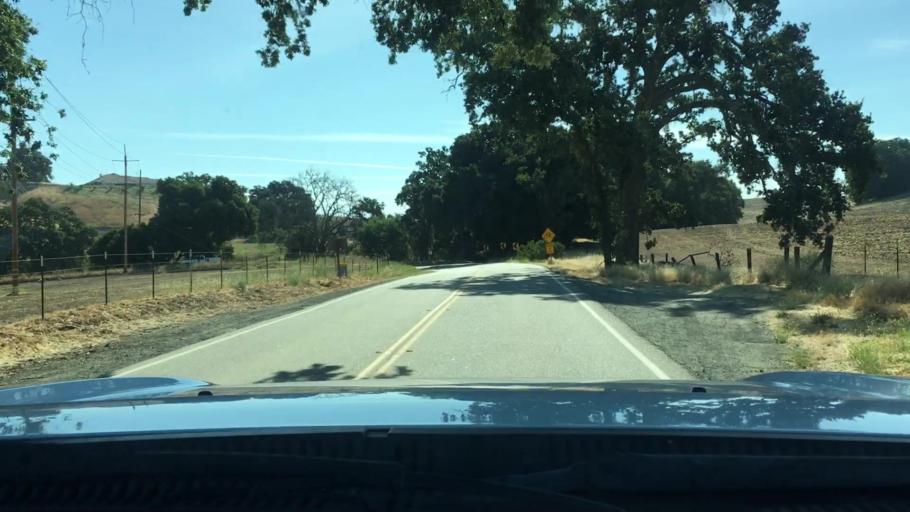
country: US
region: California
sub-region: San Luis Obispo County
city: Templeton
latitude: 35.5432
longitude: -120.7026
